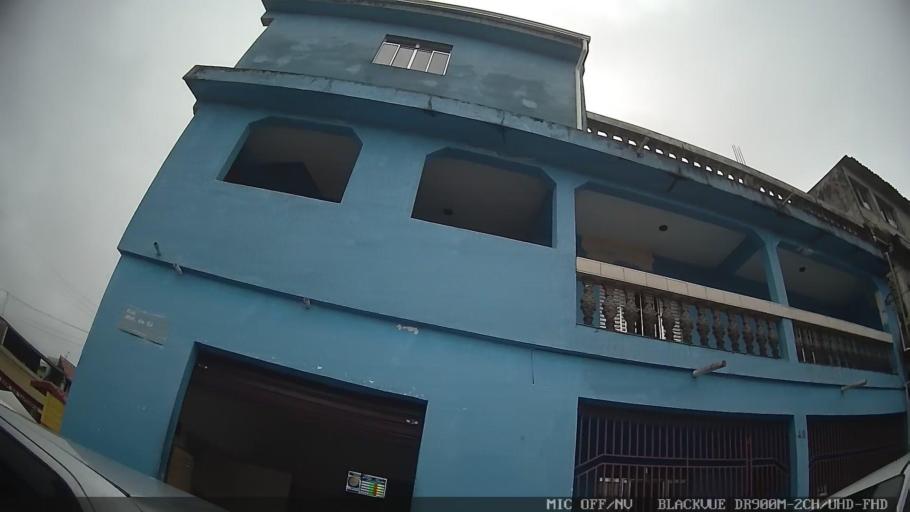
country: BR
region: Sao Paulo
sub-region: Caieiras
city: Caieiras
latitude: -23.4331
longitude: -46.7769
